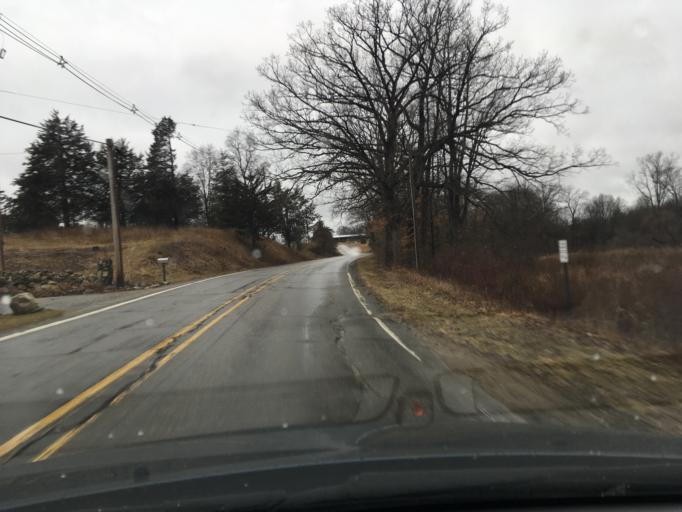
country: US
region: Michigan
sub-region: Jackson County
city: Grass Lake
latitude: 42.3109
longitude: -84.1447
